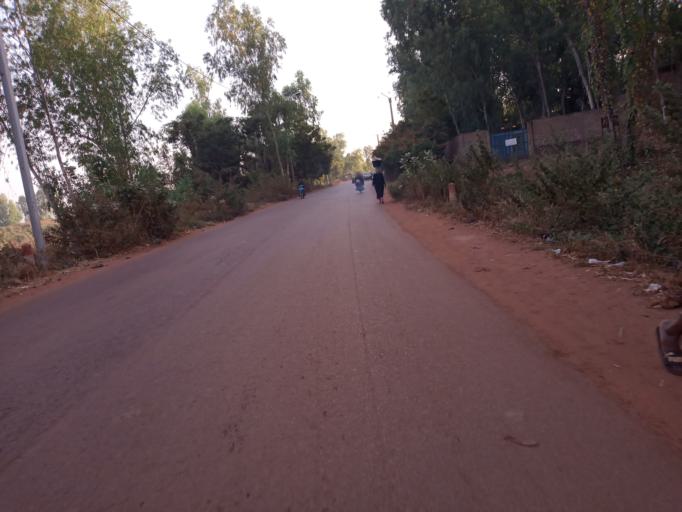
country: ML
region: Bamako
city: Bamako
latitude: 12.6308
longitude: -7.9440
